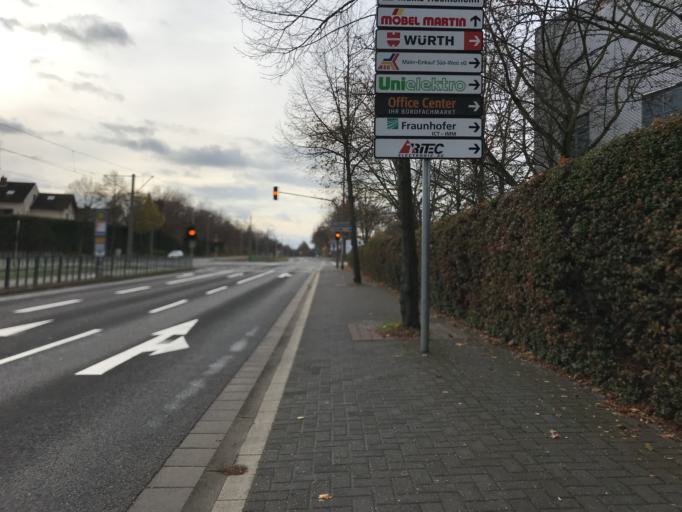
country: DE
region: Rheinland-Pfalz
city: Mainz
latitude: 49.9637
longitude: 8.2694
